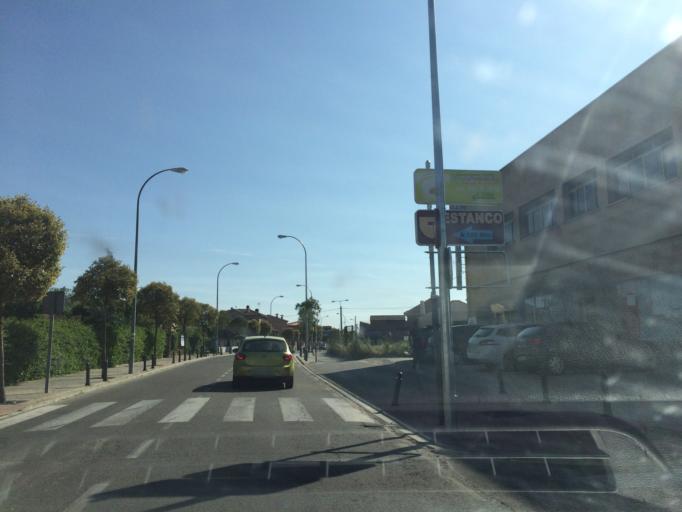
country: ES
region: Madrid
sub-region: Provincia de Madrid
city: Ribatejada
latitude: 40.7023
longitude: -3.4317
